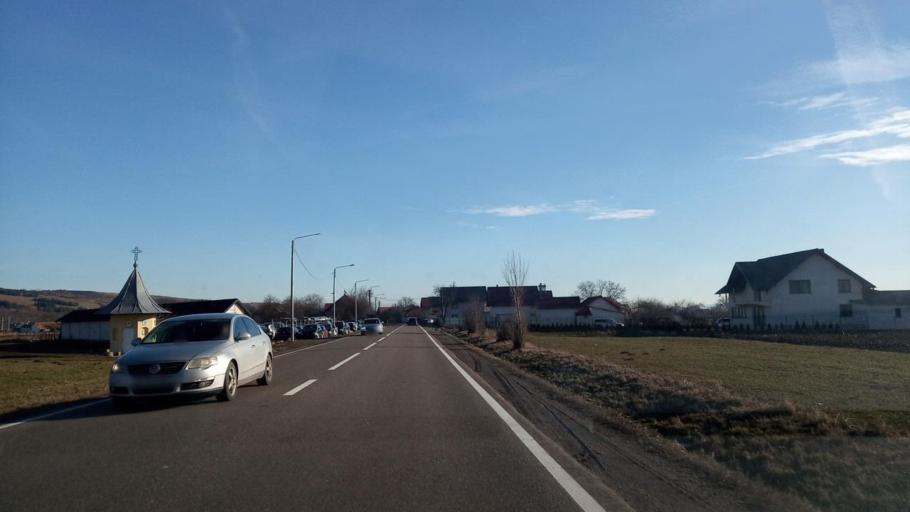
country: RO
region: Suceava
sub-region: Comuna Paltinoasa
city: Paltinoasa
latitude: 47.5376
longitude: 25.9645
